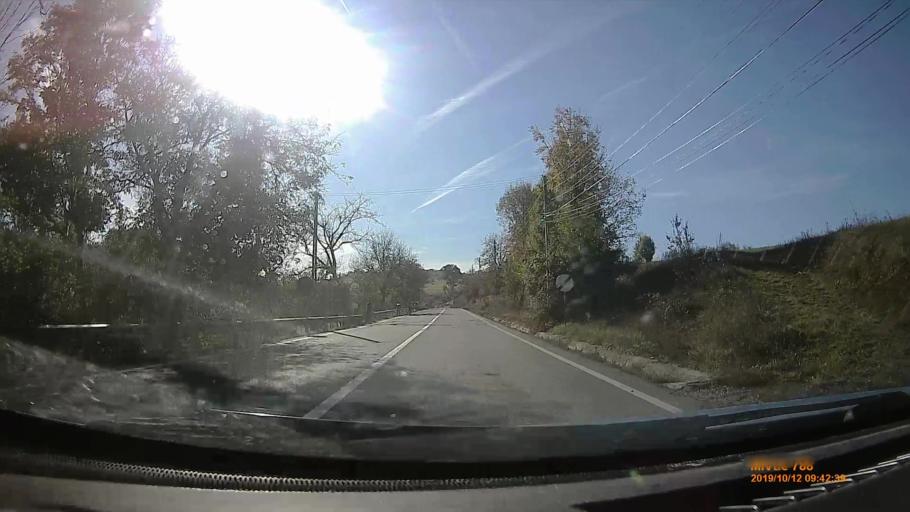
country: RO
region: Bihor
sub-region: Comuna Borod
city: Borod
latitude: 46.9809
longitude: 22.6460
